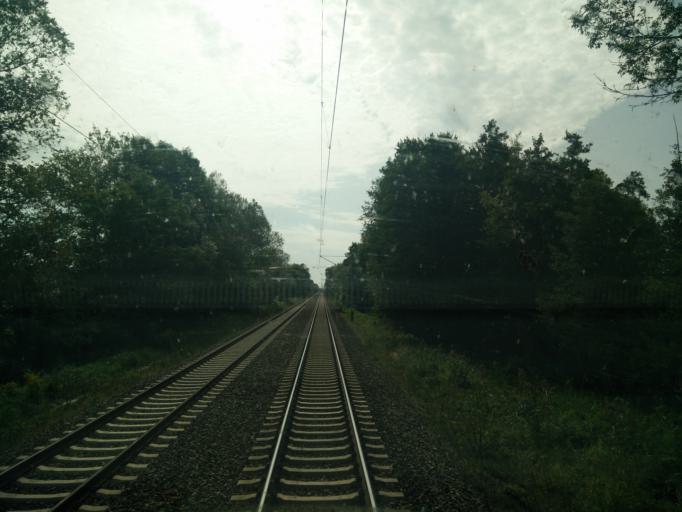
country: DE
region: Brandenburg
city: Luebben
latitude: 51.9076
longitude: 13.9021
